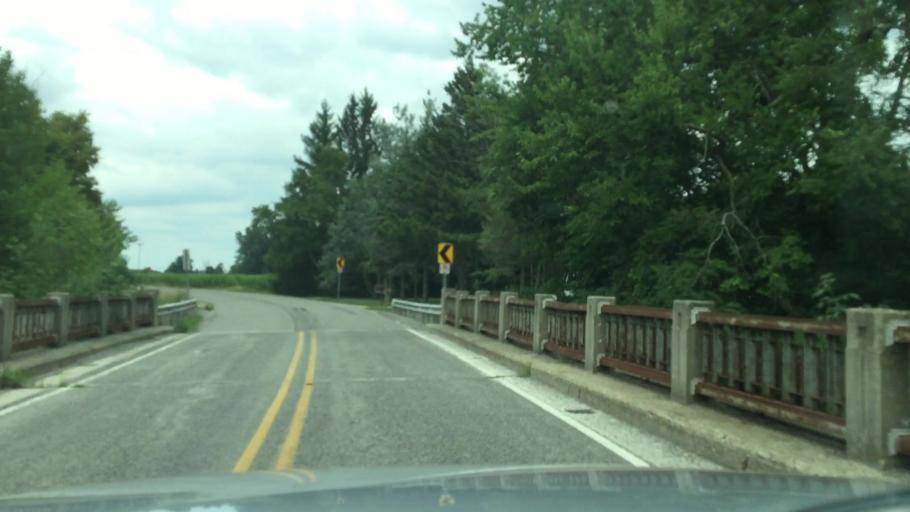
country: US
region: Michigan
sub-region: Saginaw County
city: Burt
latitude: 43.2531
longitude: -83.8667
